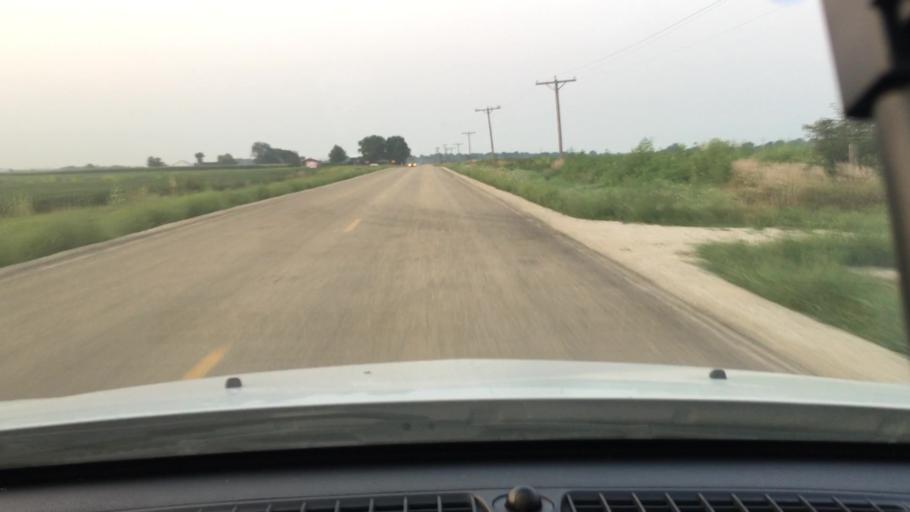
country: US
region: Illinois
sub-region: DeKalb County
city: Waterman
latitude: 41.7943
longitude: -88.7738
